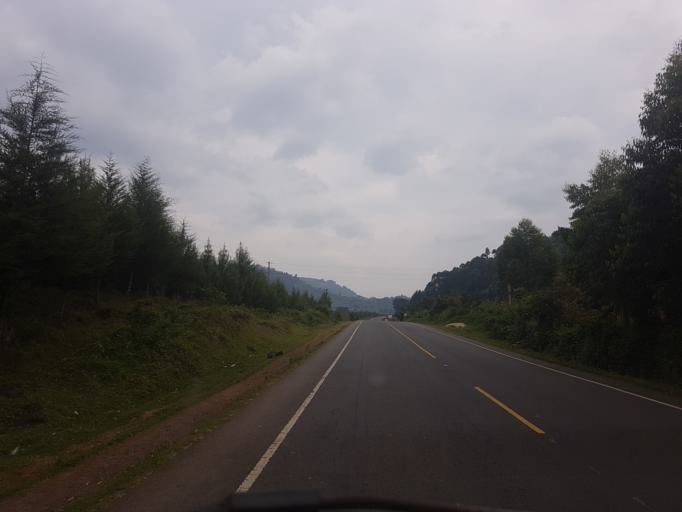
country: UG
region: Western Region
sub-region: Kisoro District
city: Kisoro
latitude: -1.2115
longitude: 29.8281
